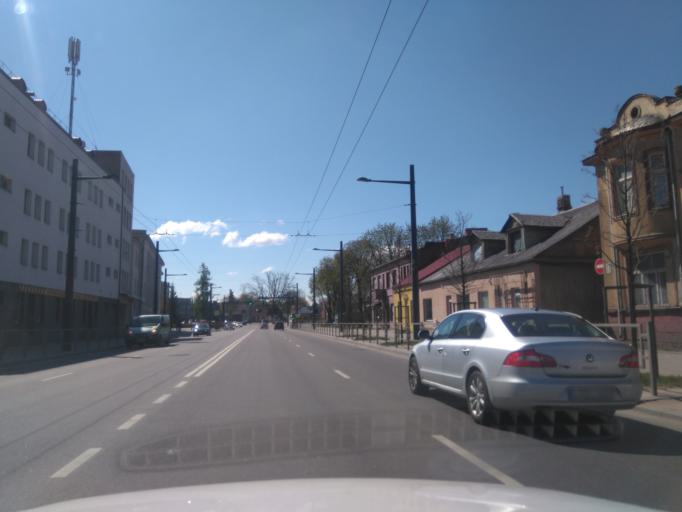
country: LT
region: Kauno apskritis
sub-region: Kaunas
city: Aleksotas
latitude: 54.8746
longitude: 23.9360
